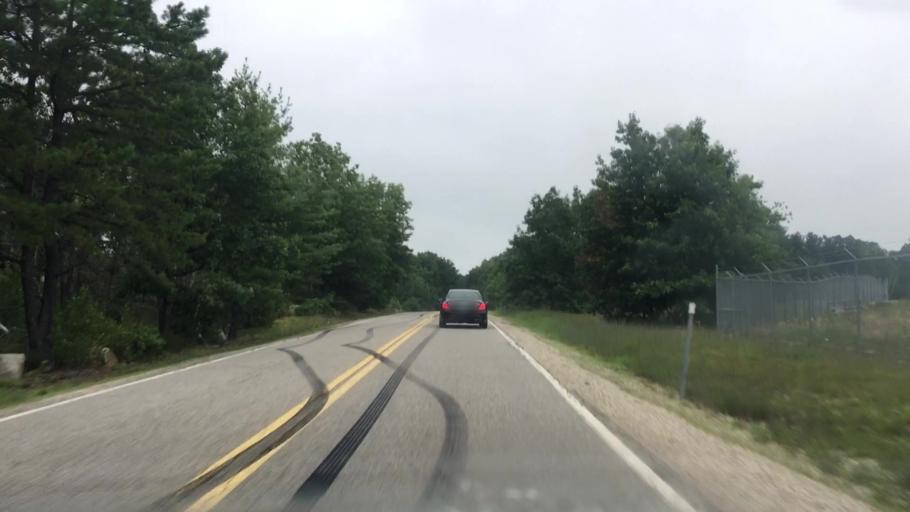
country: US
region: New Hampshire
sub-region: Rockingham County
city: Greenland
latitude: 43.0846
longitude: -70.8350
